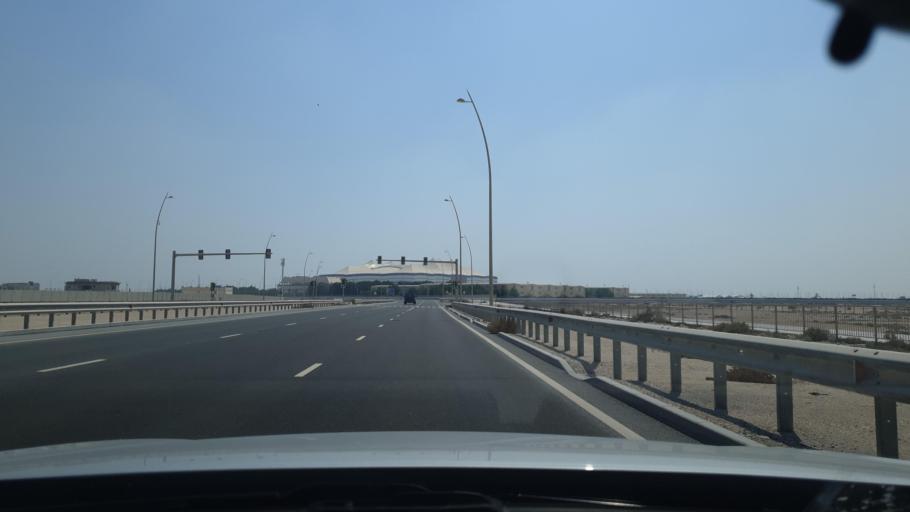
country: QA
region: Al Khawr
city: Al Khawr
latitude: 25.6635
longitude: 51.4777
